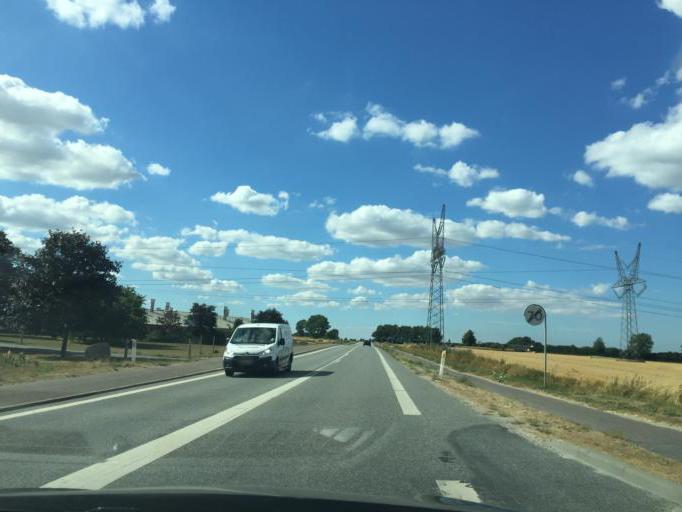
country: DK
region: South Denmark
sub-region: Odense Kommune
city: Hojby
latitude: 55.3324
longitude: 10.3920
